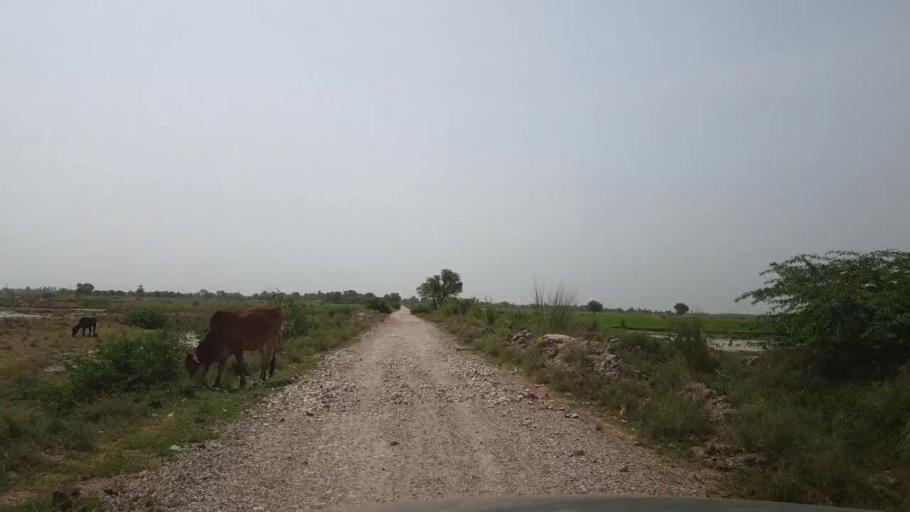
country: PK
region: Sindh
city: Madeji
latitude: 27.8330
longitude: 68.4275
